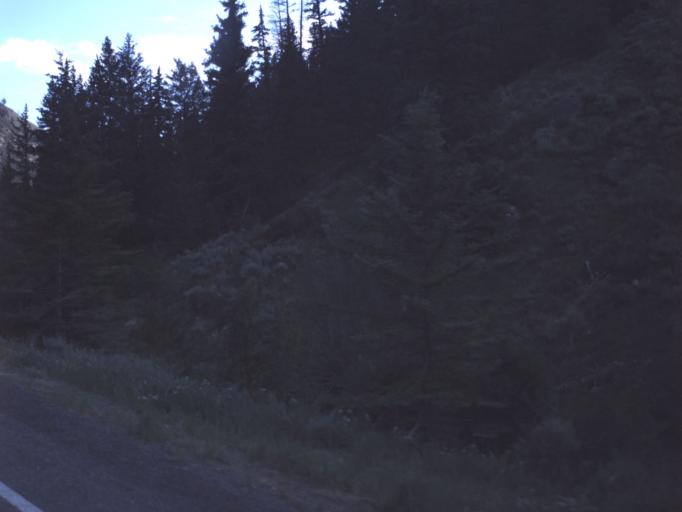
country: US
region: Utah
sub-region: Emery County
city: Huntington
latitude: 39.4822
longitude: -111.1582
